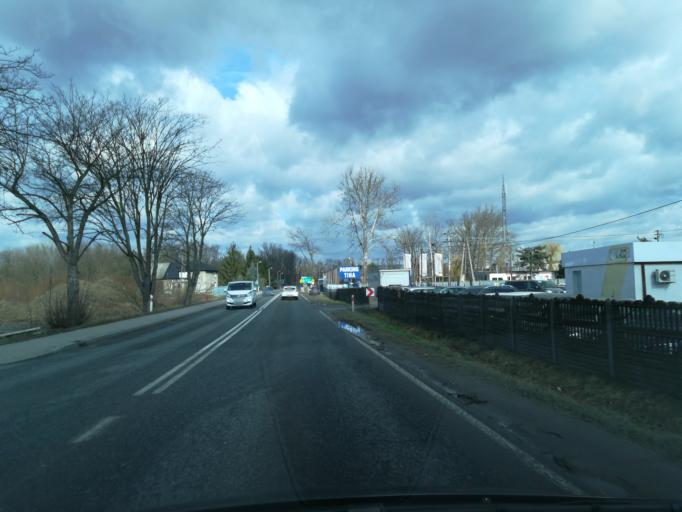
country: PL
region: Lesser Poland Voivodeship
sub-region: Powiat krakowski
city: Kryspinow
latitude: 50.0661
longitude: 19.8023
